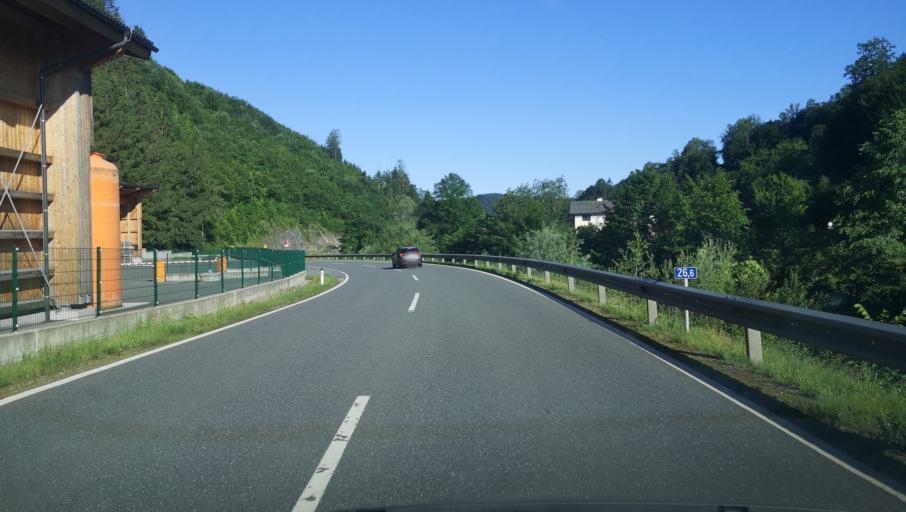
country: AT
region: Lower Austria
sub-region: Politischer Bezirk Amstetten
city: Ybbsitz
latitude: 47.9393
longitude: 14.8438
